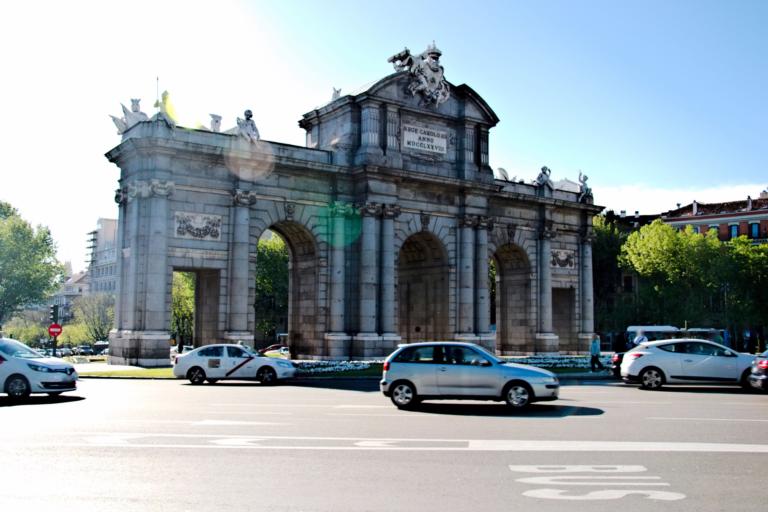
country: ES
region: Madrid
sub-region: Provincia de Madrid
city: Retiro
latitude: 40.4194
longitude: -3.6887
